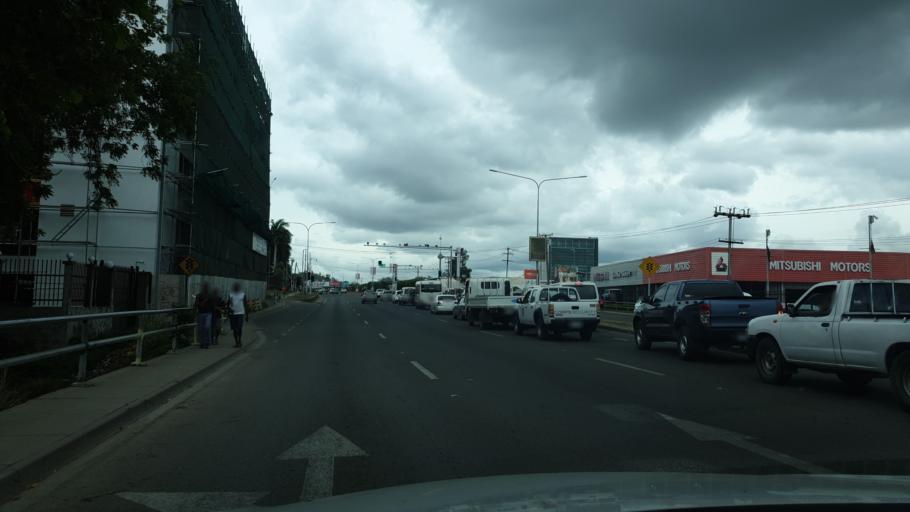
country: PG
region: National Capital
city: Port Moresby
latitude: -9.4455
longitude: 147.1831
